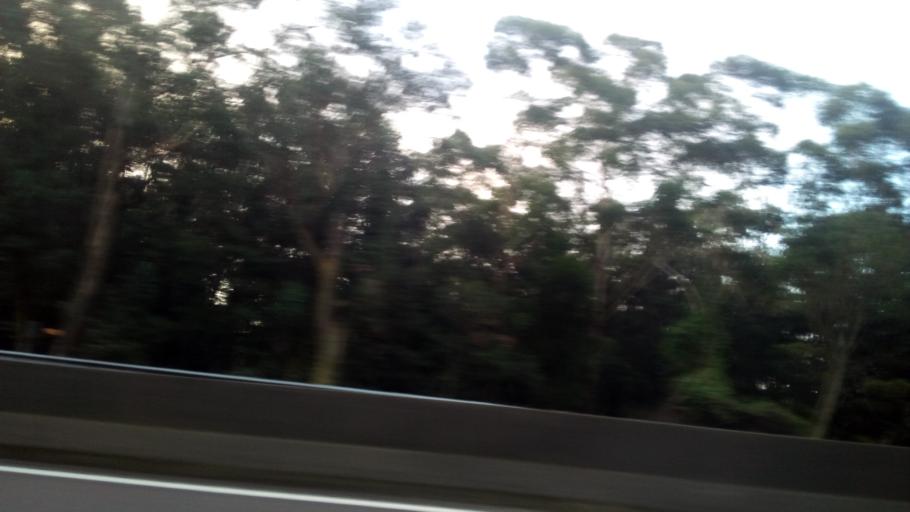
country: AU
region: New South Wales
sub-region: Wollongong
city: Bulli
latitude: -34.3460
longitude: 150.8736
